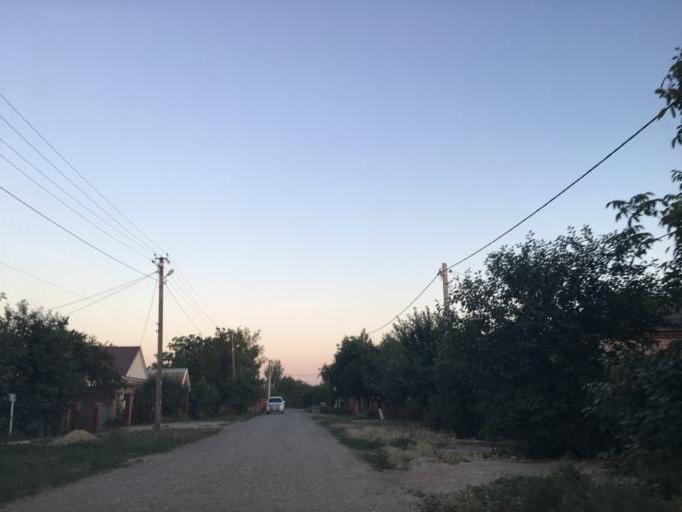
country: RU
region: Krasnodarskiy
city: Kushchevskaya
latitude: 46.5614
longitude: 39.6430
